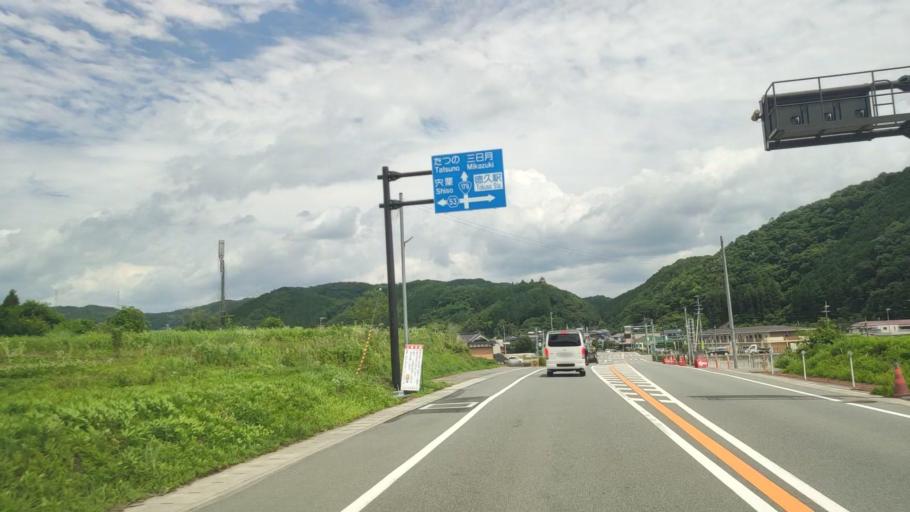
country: JP
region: Hyogo
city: Yamazakicho-nakabirose
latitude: 34.9945
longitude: 134.3929
